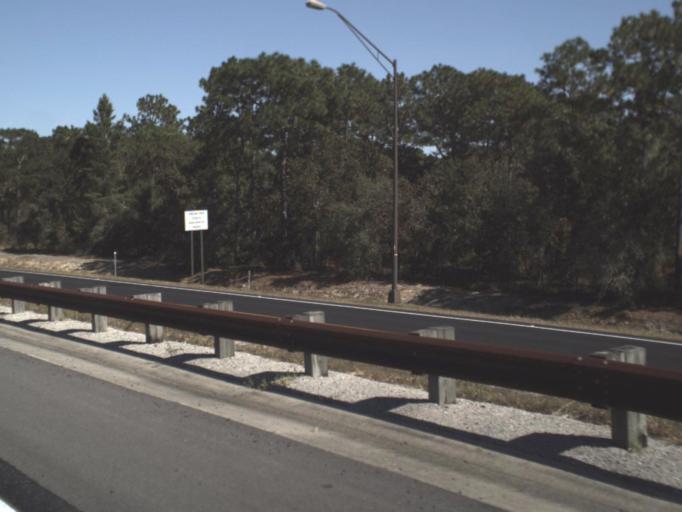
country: US
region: Florida
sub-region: Hernando County
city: Brookridge
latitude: 28.5363
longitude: -82.4793
